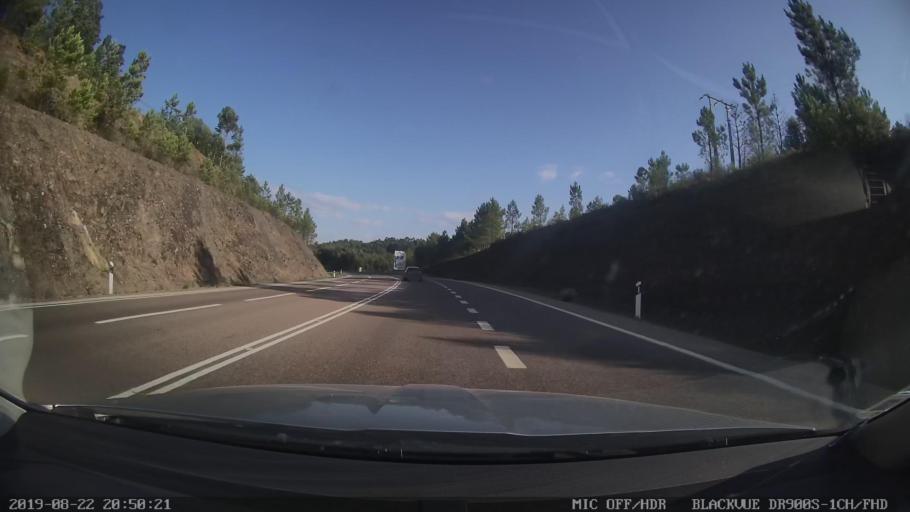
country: PT
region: Castelo Branco
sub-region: Proenca-A-Nova
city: Proenca-a-Nova
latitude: 39.7538
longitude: -7.9382
